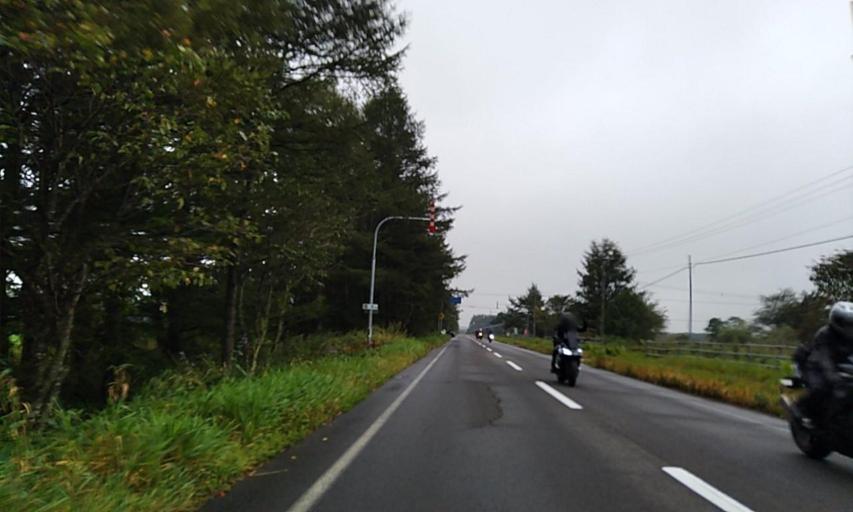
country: JP
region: Hokkaido
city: Shibetsu
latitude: 43.4952
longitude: 144.6471
